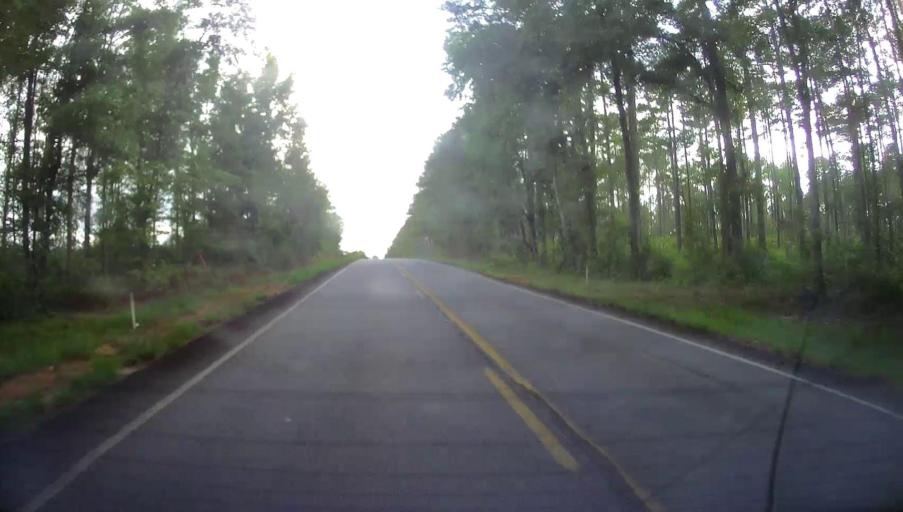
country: US
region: Georgia
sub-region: Crawford County
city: Knoxville
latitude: 32.8532
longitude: -84.0034
